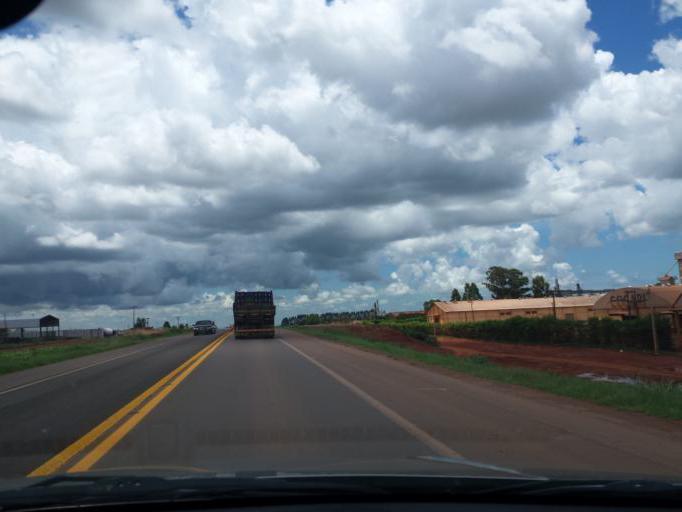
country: BR
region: Goias
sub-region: Cristalina
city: Cristalina
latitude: -16.7782
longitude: -47.6269
